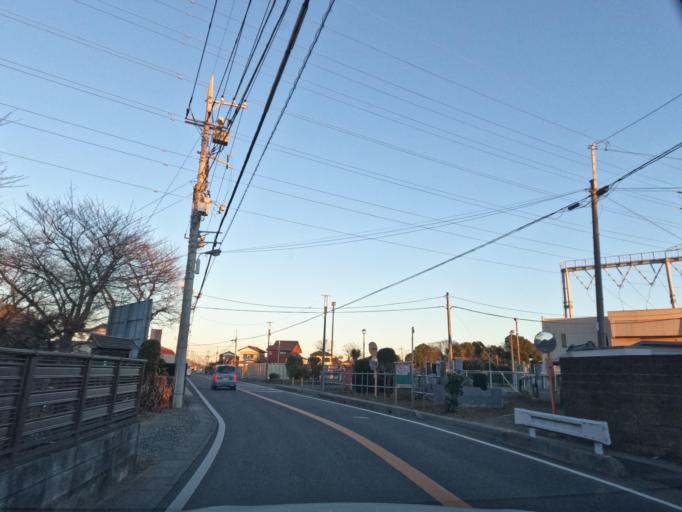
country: JP
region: Saitama
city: Kasukabe
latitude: 35.9803
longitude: 139.7161
